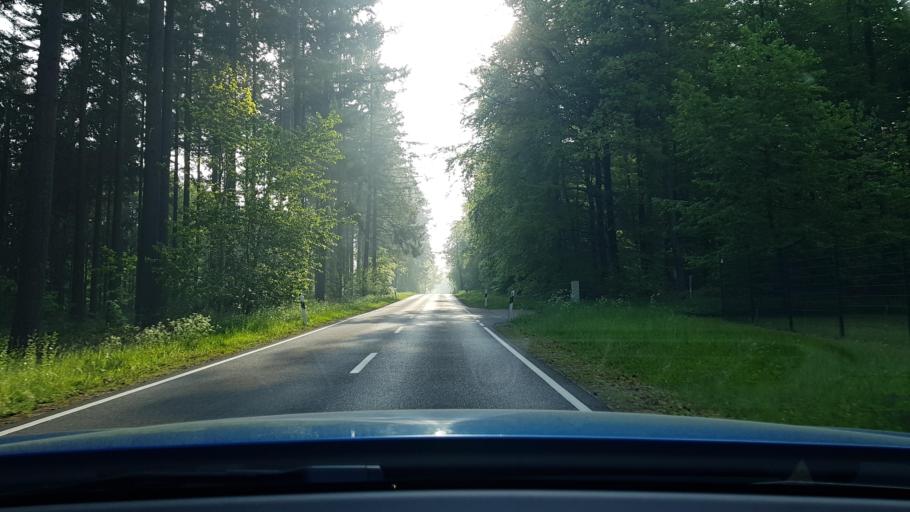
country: LU
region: Luxembourg
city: Heisdorf-sur-Alzette
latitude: 49.6588
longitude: 6.1801
